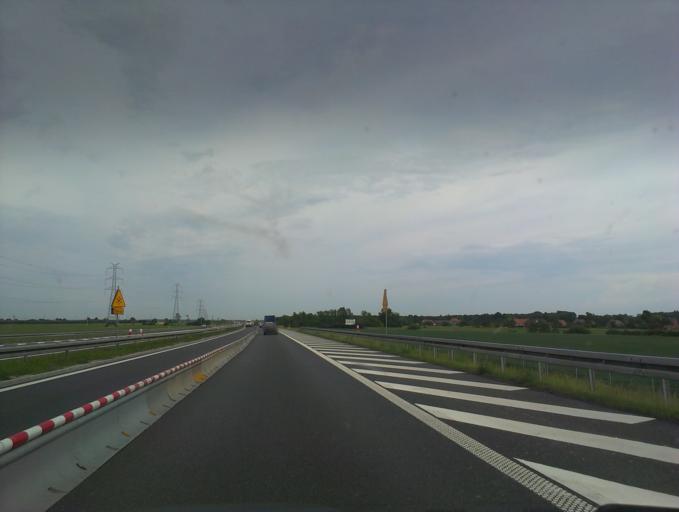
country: PL
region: Opole Voivodeship
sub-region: Powiat brzeski
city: Losiow
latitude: 50.7230
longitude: 17.5269
